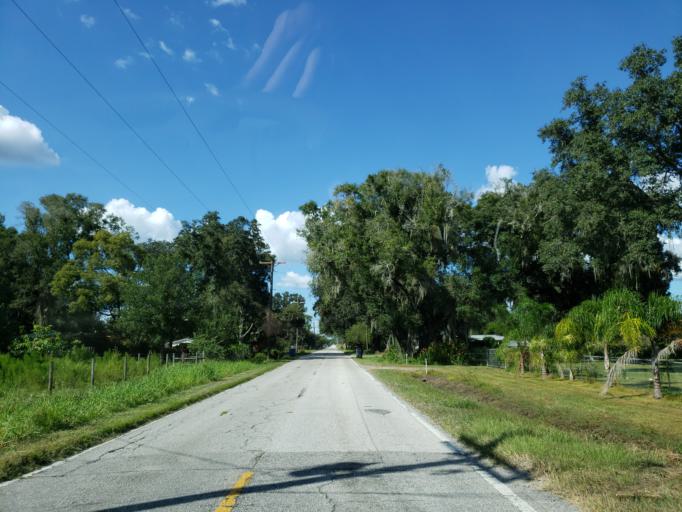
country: US
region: Florida
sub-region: Hillsborough County
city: Dover
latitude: 27.9606
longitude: -82.2031
